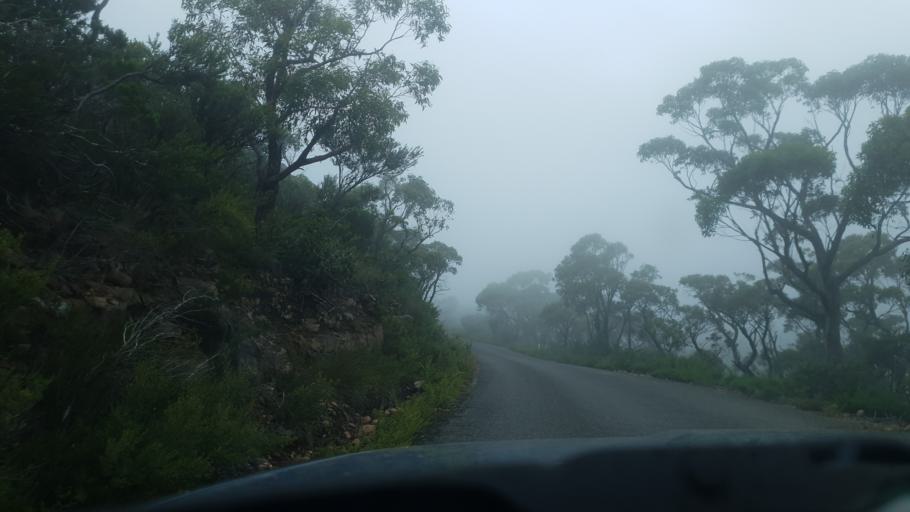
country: AU
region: Victoria
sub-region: Northern Grampians
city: Stawell
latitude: -37.2741
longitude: 142.5816
